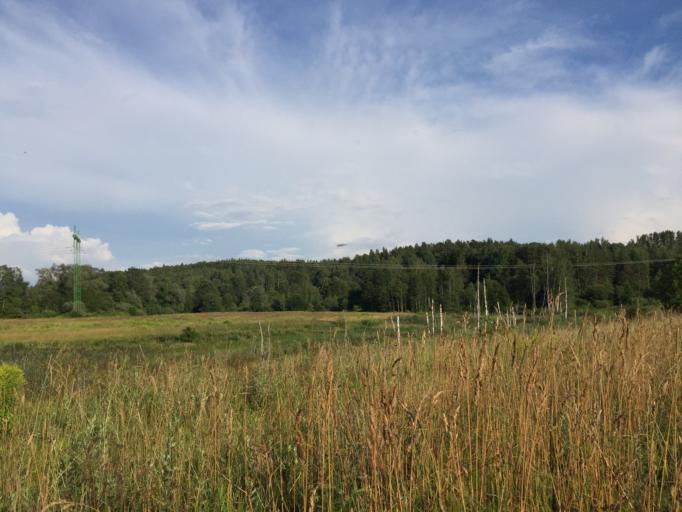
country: LV
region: Krimulda
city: Ragana
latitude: 57.1468
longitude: 24.7597
